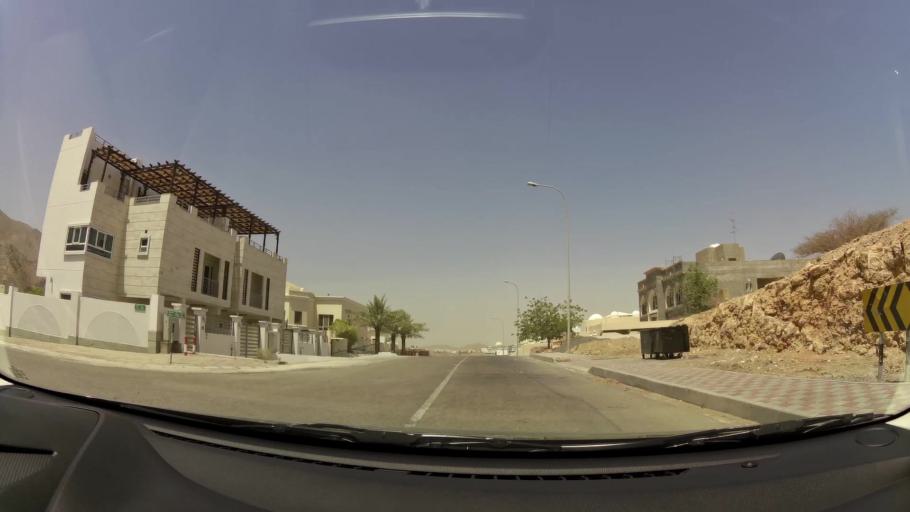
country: OM
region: Muhafazat Masqat
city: Bawshar
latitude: 23.5855
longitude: 58.4503
